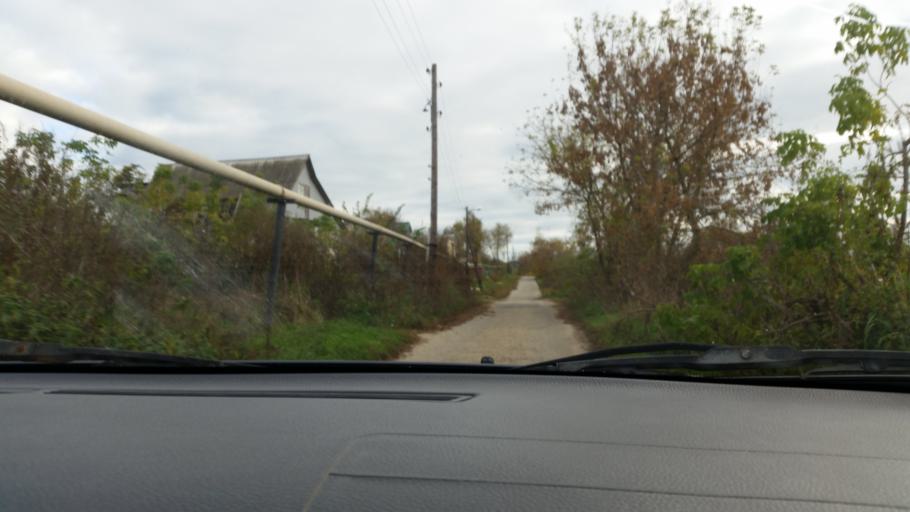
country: RU
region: Lipetsk
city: Gryazi
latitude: 52.4523
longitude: 39.9830
